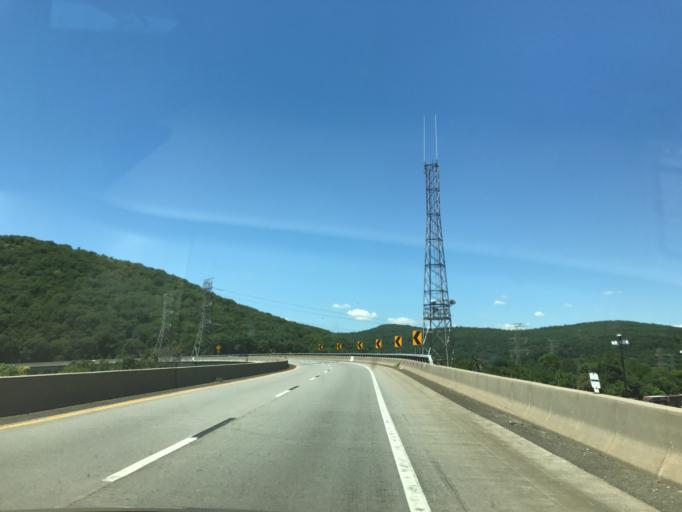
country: US
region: New York
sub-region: Rockland County
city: Suffern
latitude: 41.1184
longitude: -74.1578
